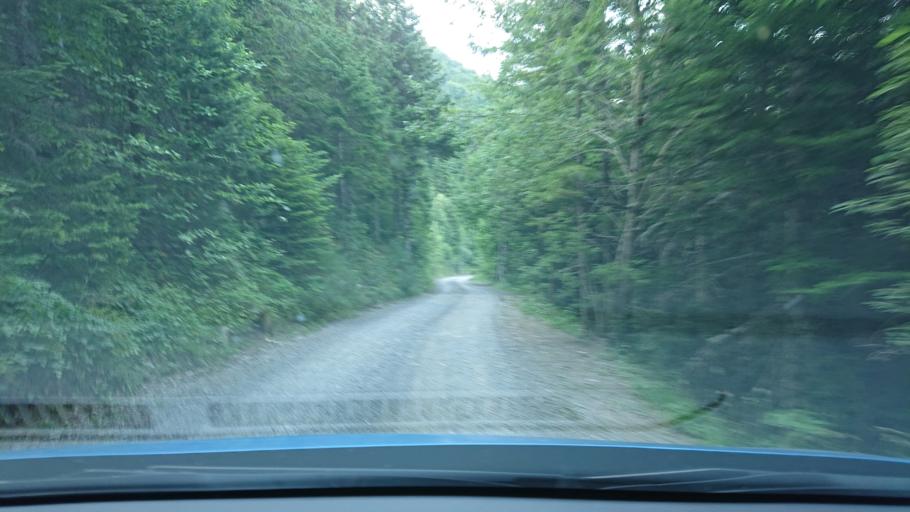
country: FR
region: Rhone-Alpes
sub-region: Departement de l'Isere
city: Mens
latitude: 44.7909
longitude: 5.8862
